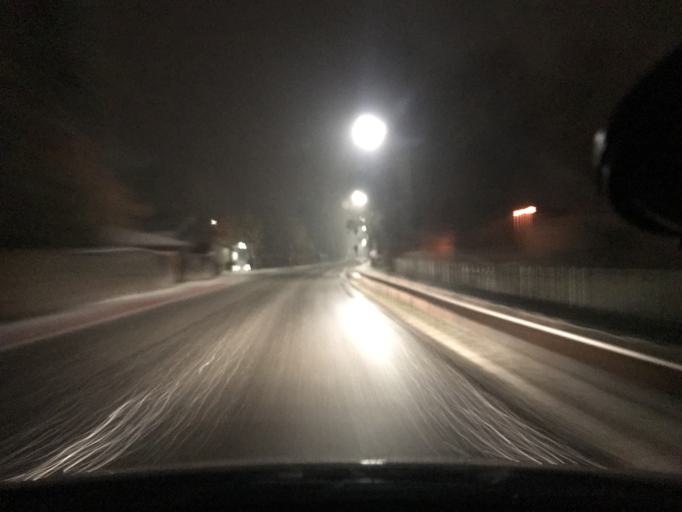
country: DE
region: Bavaria
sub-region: Upper Bavaria
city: Rosenheim
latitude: 47.8327
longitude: 12.1117
